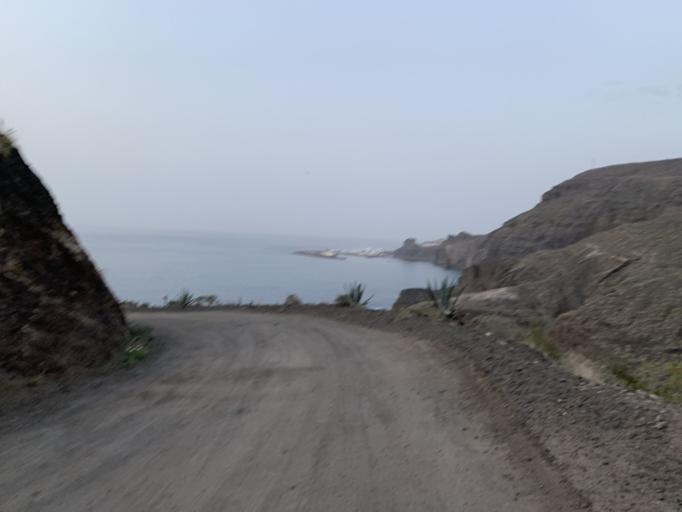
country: ES
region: Canary Islands
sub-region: Provincia de Las Palmas
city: Agaete
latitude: 28.0837
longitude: -15.7086
